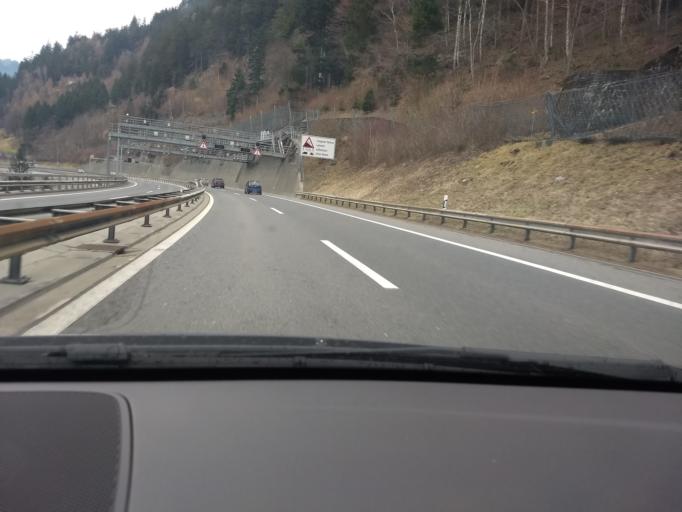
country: CH
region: Uri
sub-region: Uri
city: Silenen
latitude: 46.7439
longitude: 8.6430
